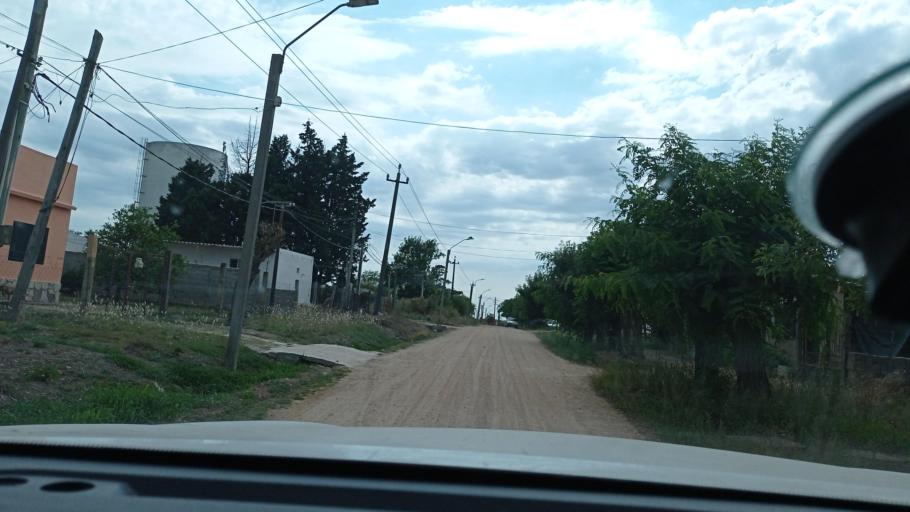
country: UY
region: Canelones
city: Pando
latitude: -34.7064
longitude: -55.9683
